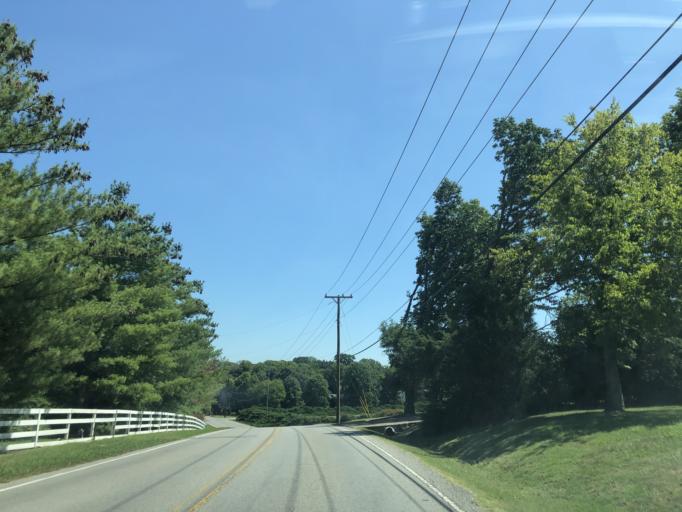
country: US
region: Tennessee
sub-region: Davidson County
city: Oak Hill
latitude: 36.0780
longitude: -86.7839
